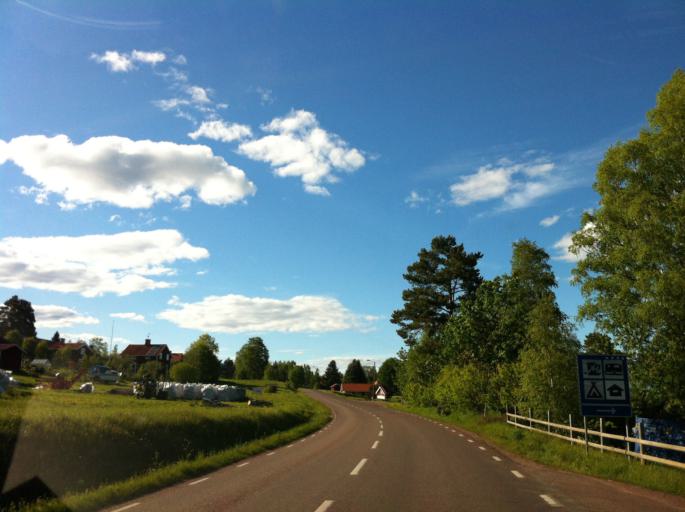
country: SE
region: Dalarna
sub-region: Leksand Municipality
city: Leksand
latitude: 60.7297
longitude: 14.9515
